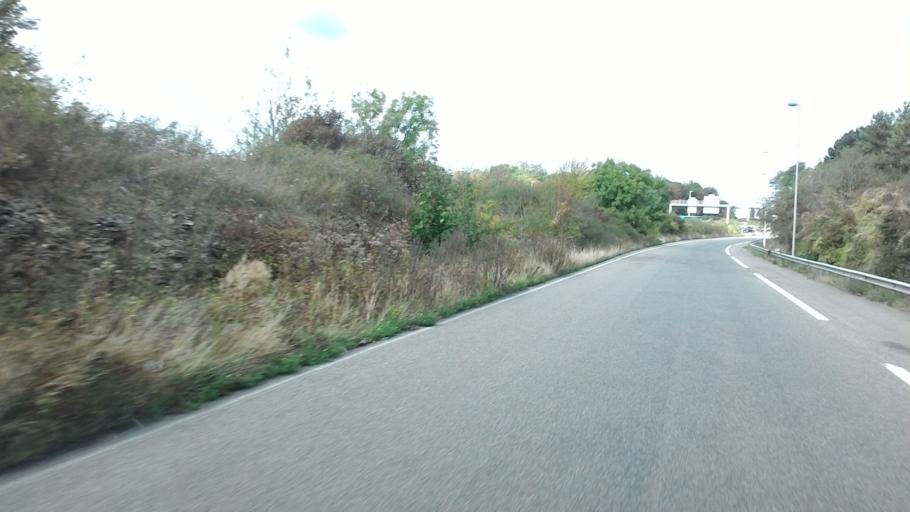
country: FR
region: Lorraine
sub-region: Departement de Meurthe-et-Moselle
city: Laxou
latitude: 48.6961
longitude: 6.1191
